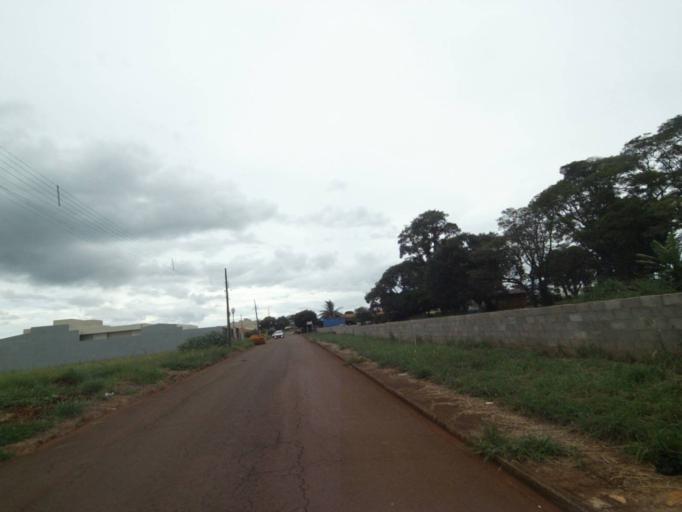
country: BR
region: Parana
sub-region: Campo Mourao
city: Campo Mourao
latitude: -24.0317
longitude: -52.3632
